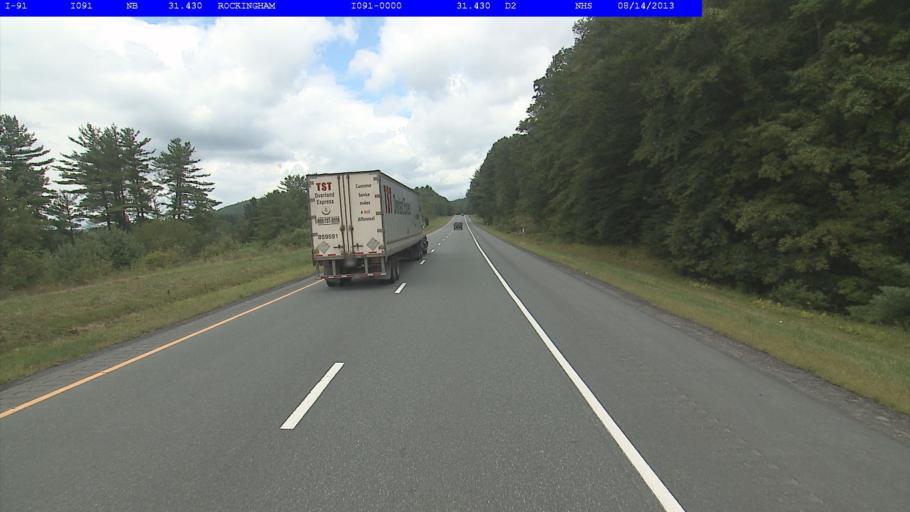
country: US
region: Vermont
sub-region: Windham County
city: Bellows Falls
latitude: 43.1276
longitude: -72.4721
